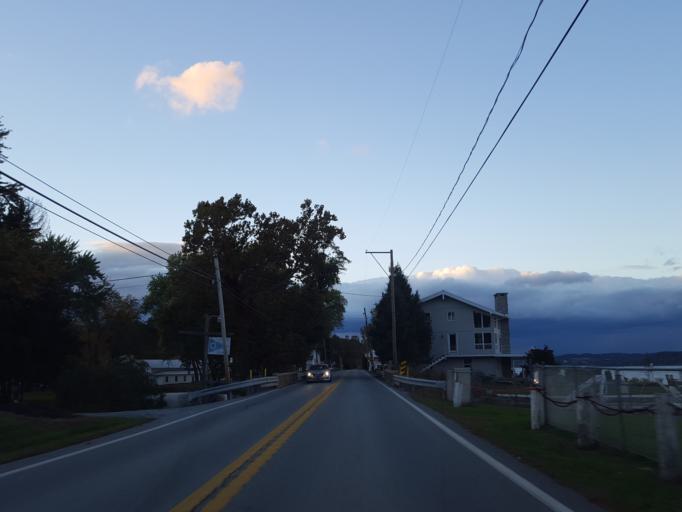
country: US
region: Pennsylvania
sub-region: Lancaster County
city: Columbia
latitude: 39.9696
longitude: -76.4919
